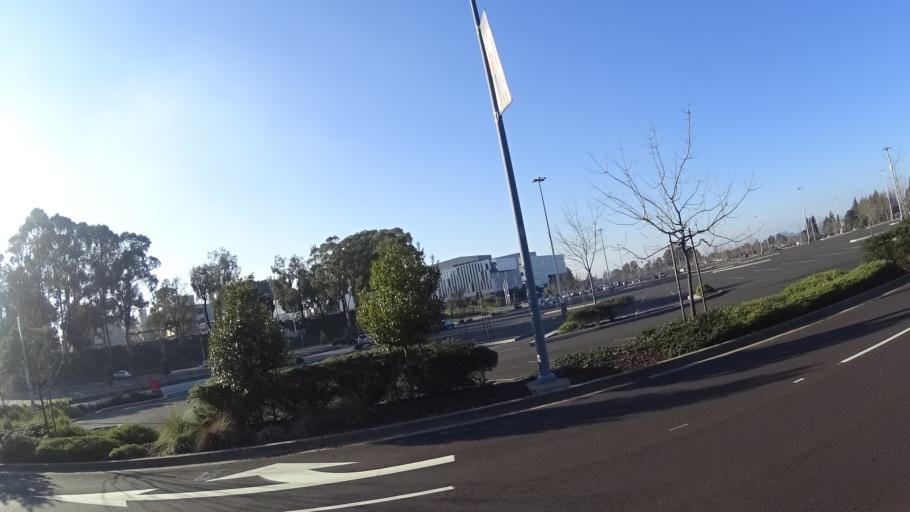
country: US
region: California
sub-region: Alameda County
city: Fairview
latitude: 37.6569
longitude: -122.0513
